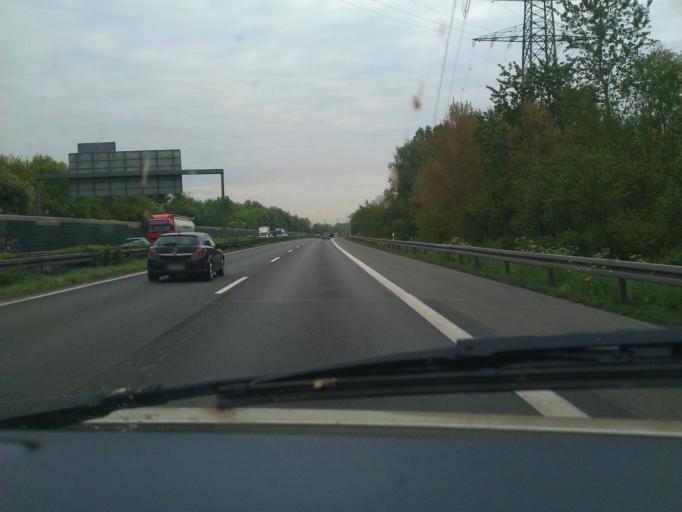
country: DE
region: North Rhine-Westphalia
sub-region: Regierungsbezirk Munster
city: Bottrop
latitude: 51.5655
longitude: 6.9292
